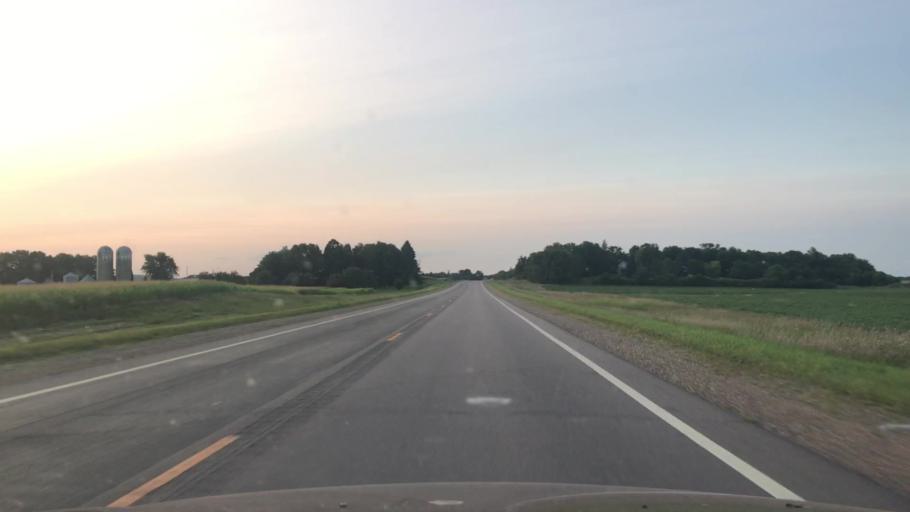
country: US
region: Minnesota
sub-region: Redwood County
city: Redwood Falls
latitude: 44.5146
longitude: -95.1181
